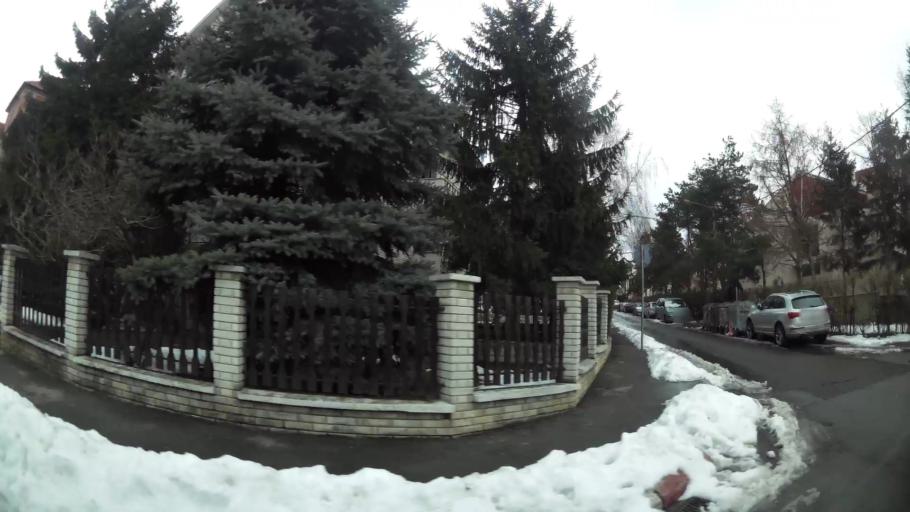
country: RS
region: Central Serbia
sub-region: Belgrade
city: Rakovica
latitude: 44.7524
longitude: 20.4201
